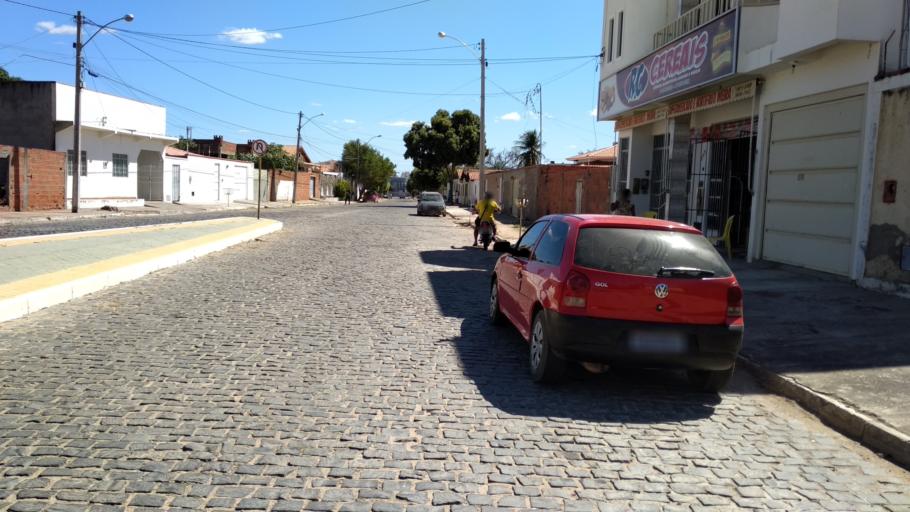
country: BR
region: Bahia
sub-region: Guanambi
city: Guanambi
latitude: -14.2345
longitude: -42.7765
